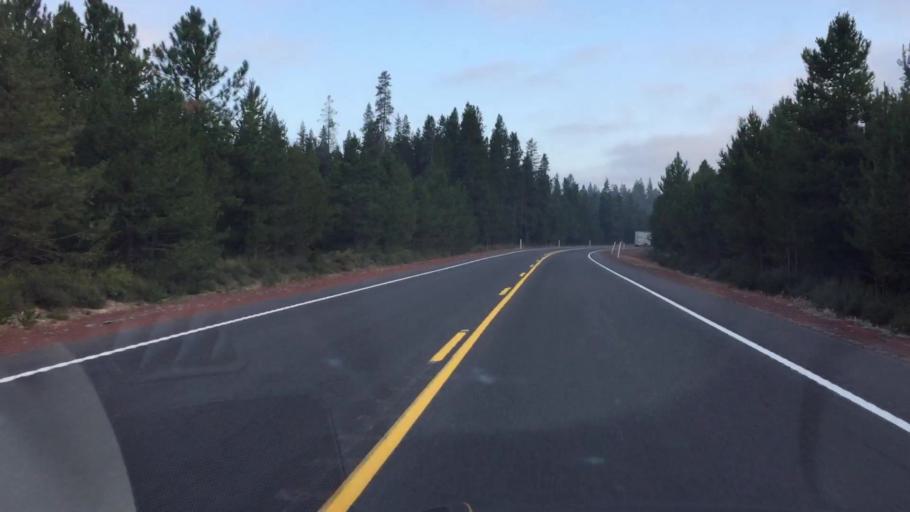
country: US
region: Oregon
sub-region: Deschutes County
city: La Pine
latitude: 43.3083
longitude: -121.7672
